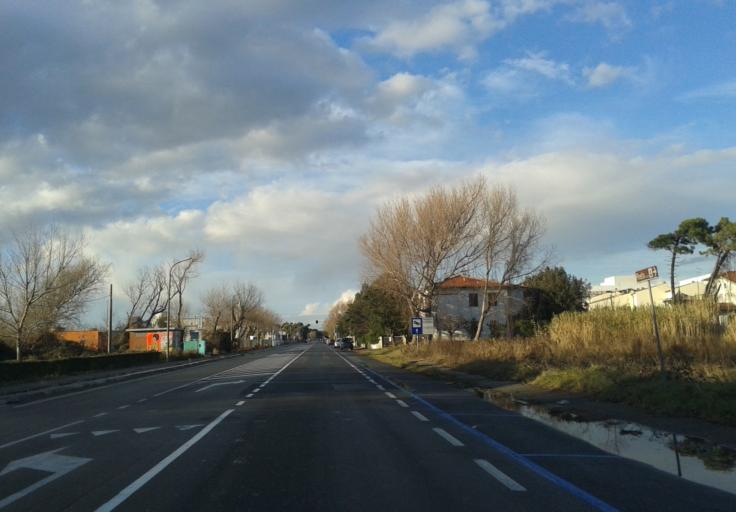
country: IT
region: Tuscany
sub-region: Province of Pisa
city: Marina di Pisa-Tirrenia-Calambrone
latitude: 43.5890
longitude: 10.2990
